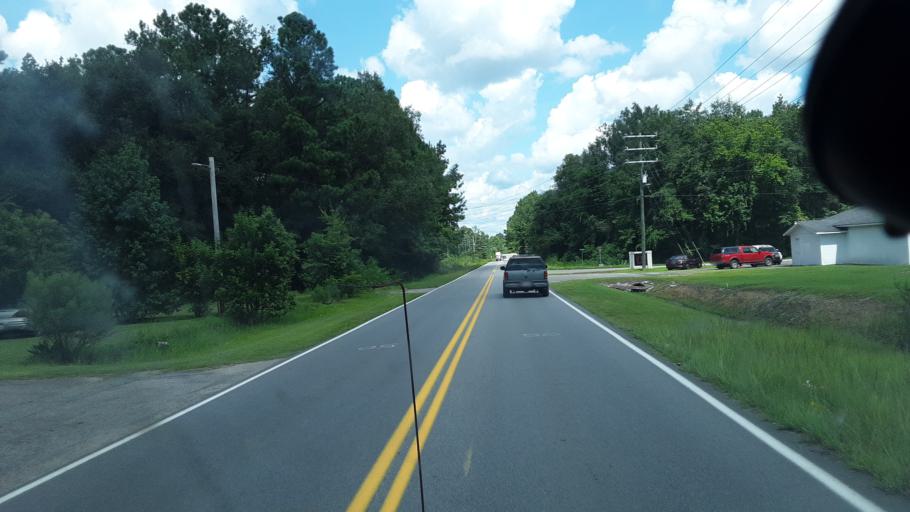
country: US
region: South Carolina
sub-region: Williamsburg County
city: Andrews
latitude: 33.4680
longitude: -79.5652
